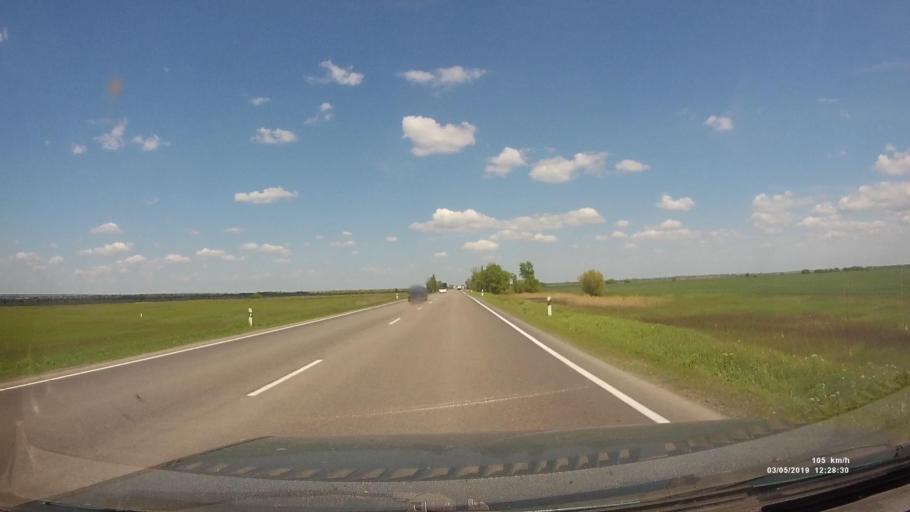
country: RU
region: Rostov
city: Semikarakorsk
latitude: 47.4743
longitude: 40.7285
